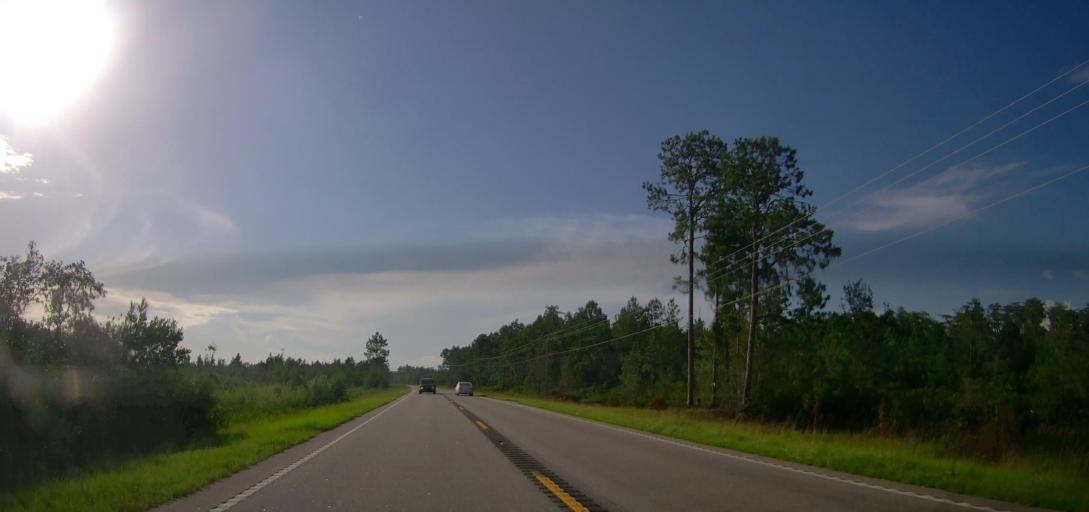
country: US
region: Georgia
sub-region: Coffee County
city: Nicholls
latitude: 31.3816
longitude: -82.6447
